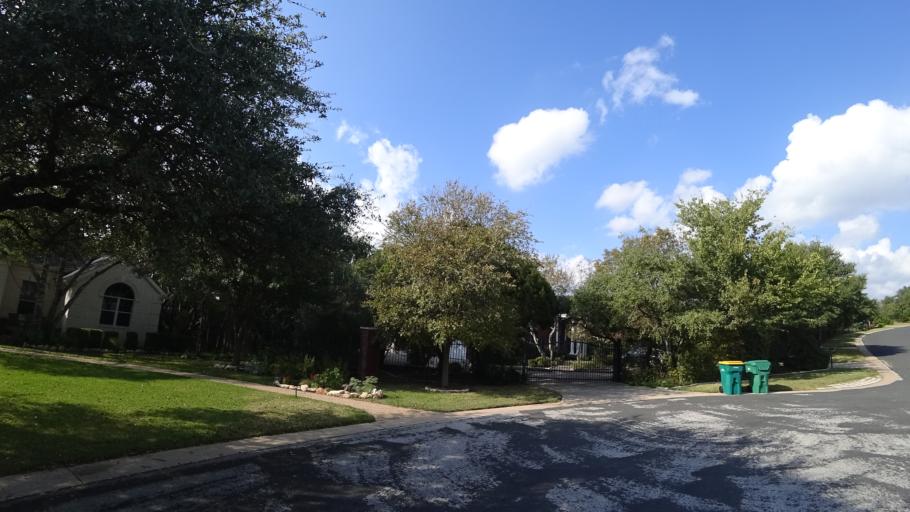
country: US
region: Texas
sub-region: Travis County
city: Lost Creek
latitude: 30.3011
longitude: -97.8484
